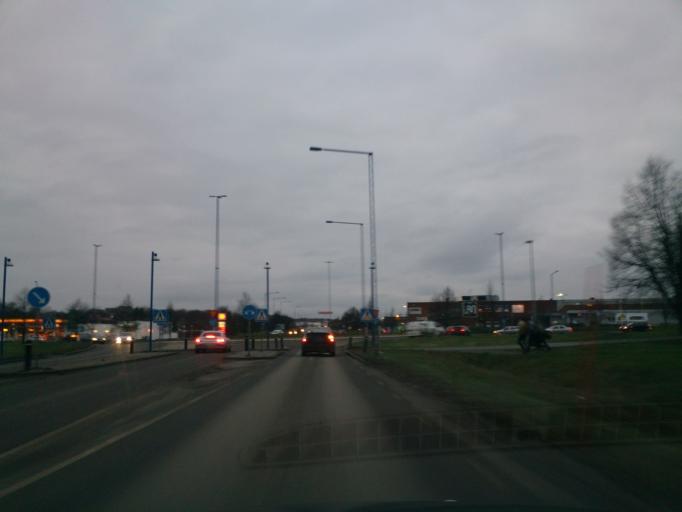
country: SE
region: OEstergoetland
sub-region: Norrkopings Kommun
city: Norrkoping
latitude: 58.6058
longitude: 16.1778
